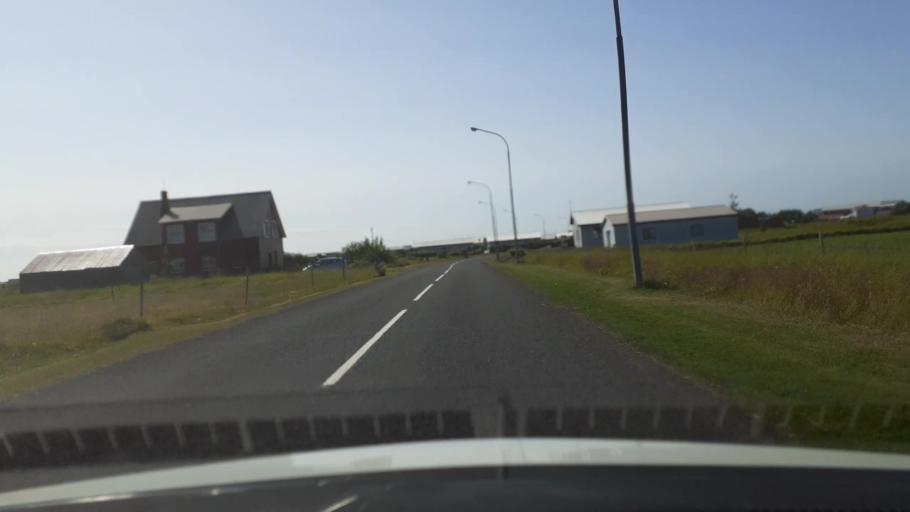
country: IS
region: South
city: Selfoss
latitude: 63.8405
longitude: -21.0540
